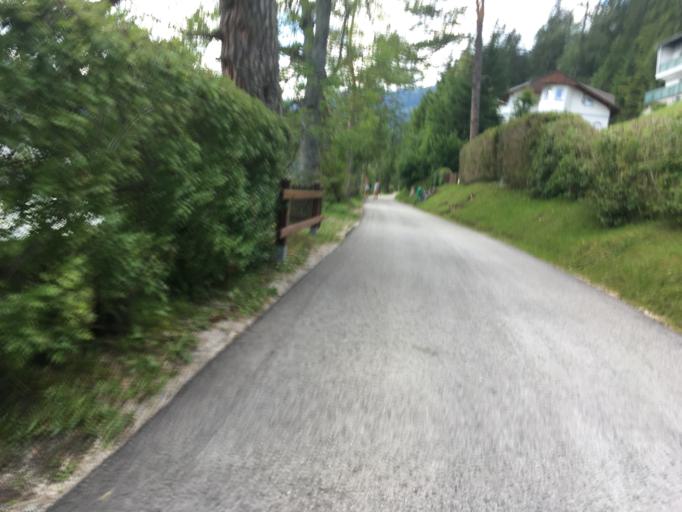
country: AT
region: Lower Austria
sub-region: Politischer Bezirk Lilienfeld
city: Mitterbach am Erlaufsee
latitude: 47.7930
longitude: 15.2767
